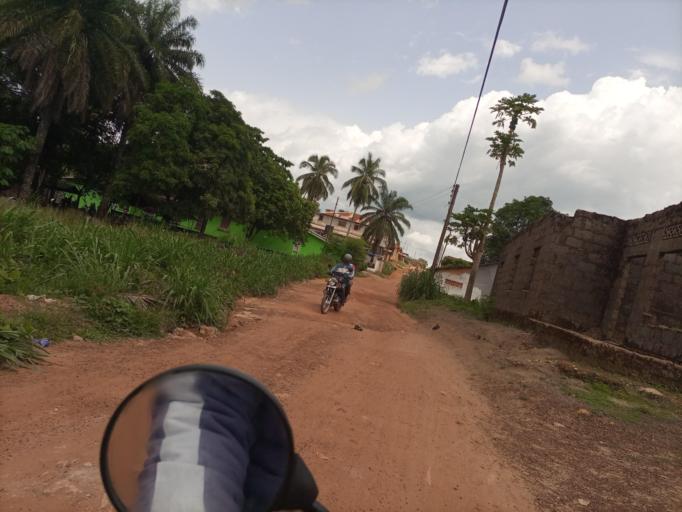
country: SL
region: Southern Province
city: Bo
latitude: 7.9489
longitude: -11.7365
